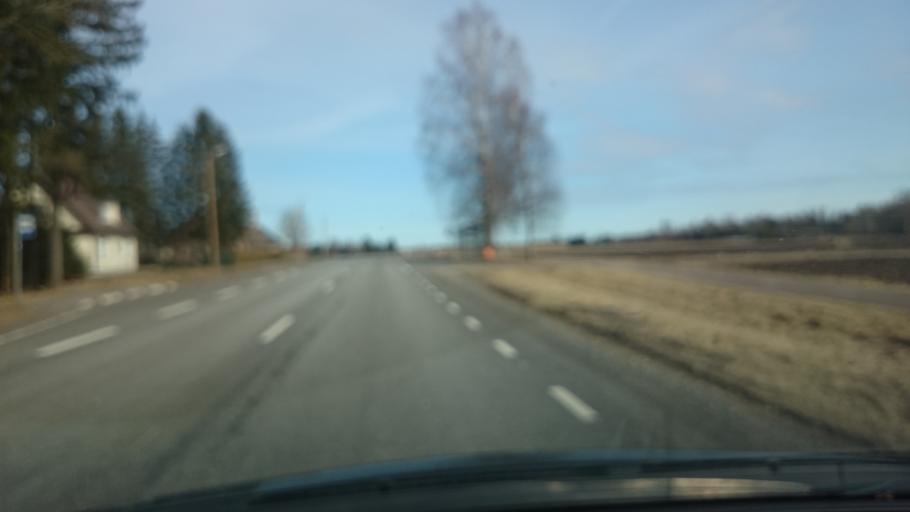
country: EE
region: Jaervamaa
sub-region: Paide linn
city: Paide
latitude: 58.8899
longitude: 25.4866
